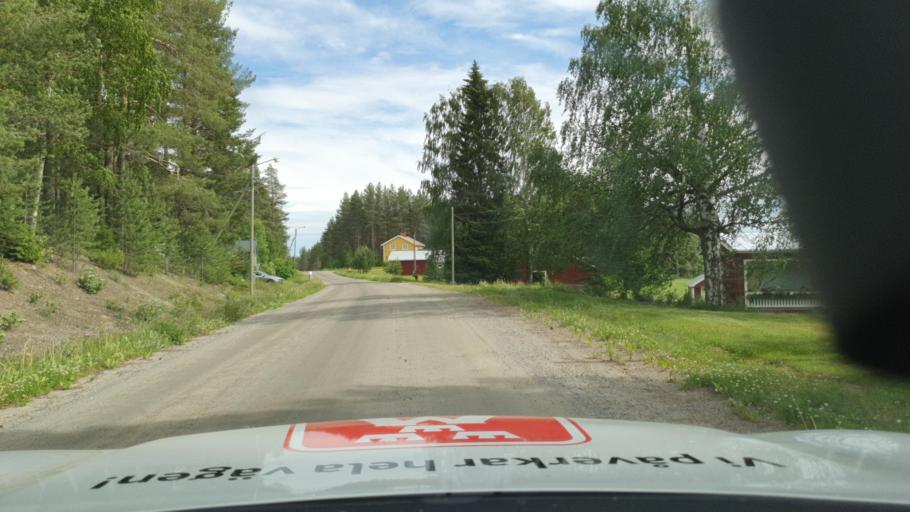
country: SE
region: Vaesterbotten
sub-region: Skelleftea Kommun
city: Burtraesk
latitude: 64.4890
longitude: 20.6104
